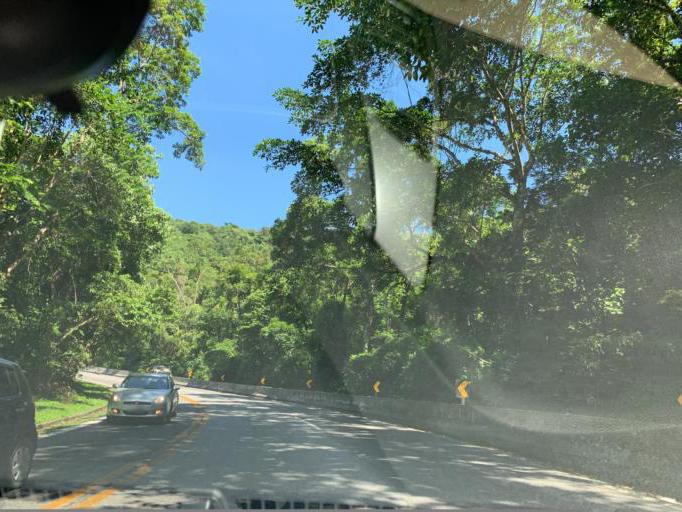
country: BR
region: Sao Paulo
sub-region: Bertioga
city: Bertioga
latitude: -23.7495
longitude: -46.0389
